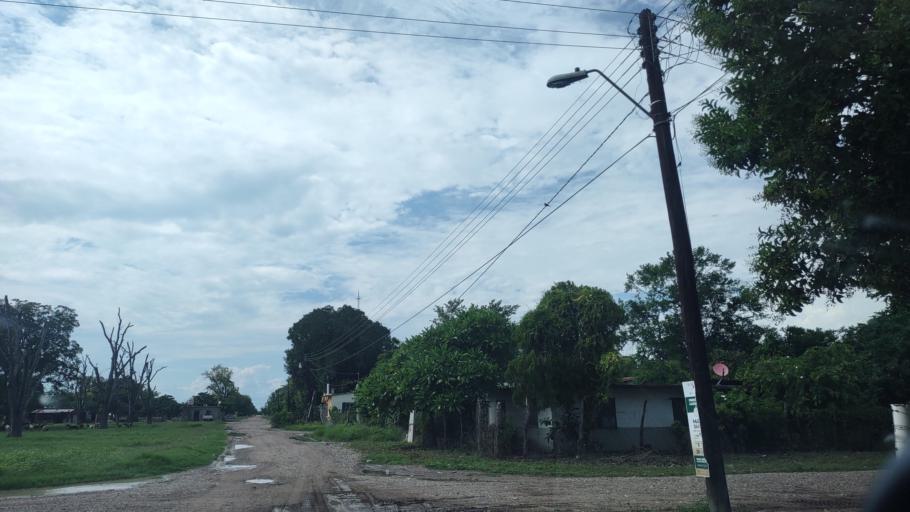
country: MX
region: Veracruz
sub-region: Panuco
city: Oviedo
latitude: 22.0031
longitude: -98.4567
